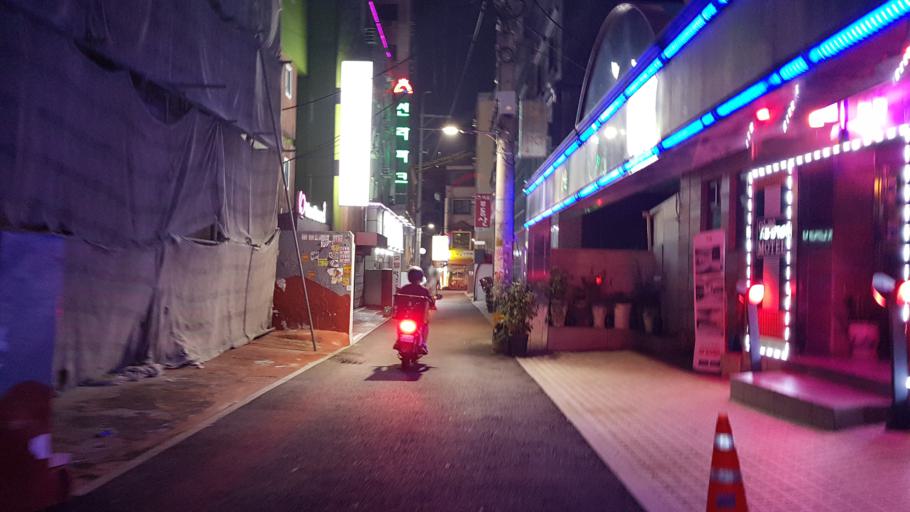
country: KR
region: Gyeonggi-do
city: Kwangmyong
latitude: 37.4843
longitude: 126.9276
